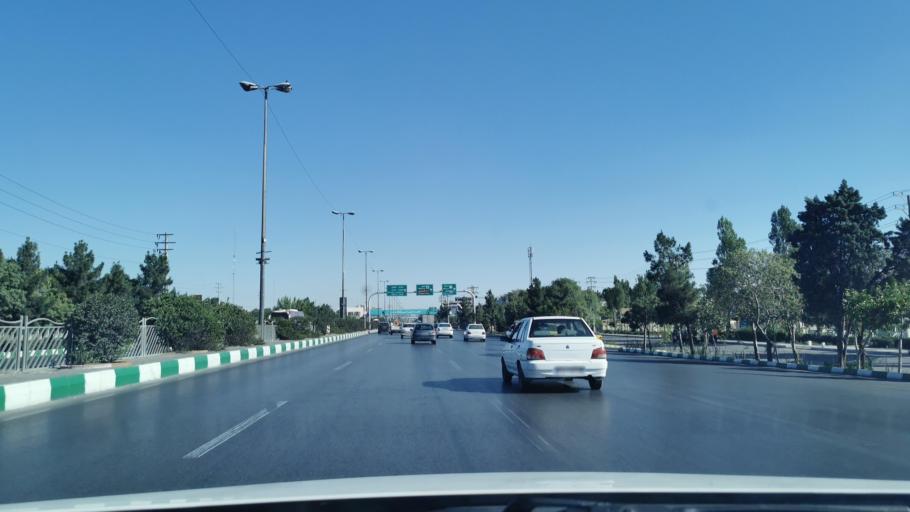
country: IR
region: Razavi Khorasan
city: Mashhad
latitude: 36.3502
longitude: 59.5457
